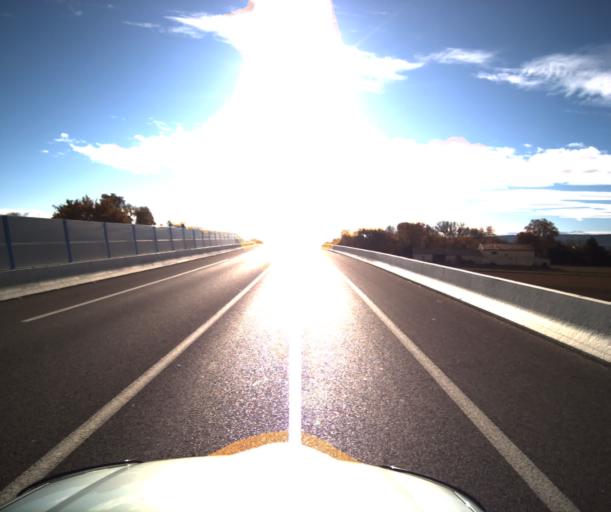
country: FR
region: Provence-Alpes-Cote d'Azur
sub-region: Departement du Vaucluse
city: Pertuis
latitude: 43.6849
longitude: 5.4838
